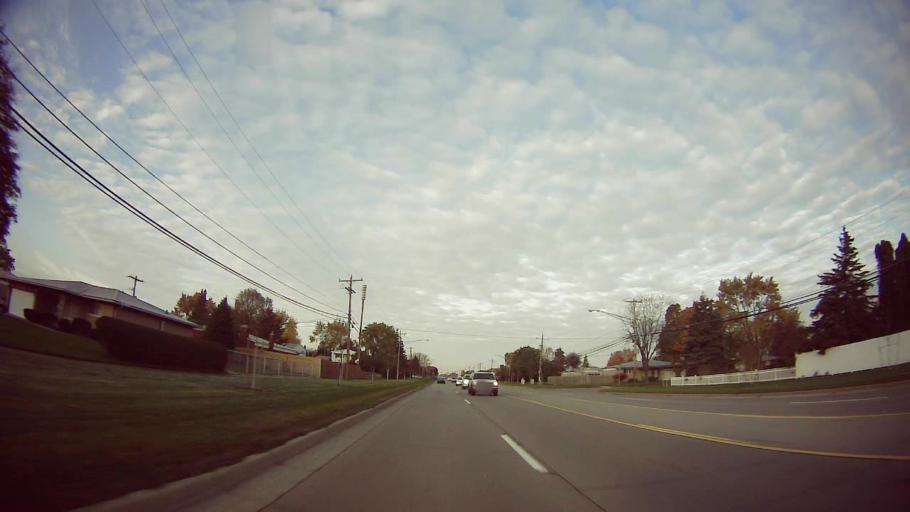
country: US
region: Michigan
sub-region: Macomb County
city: Sterling Heights
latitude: 42.5514
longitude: -83.0170
